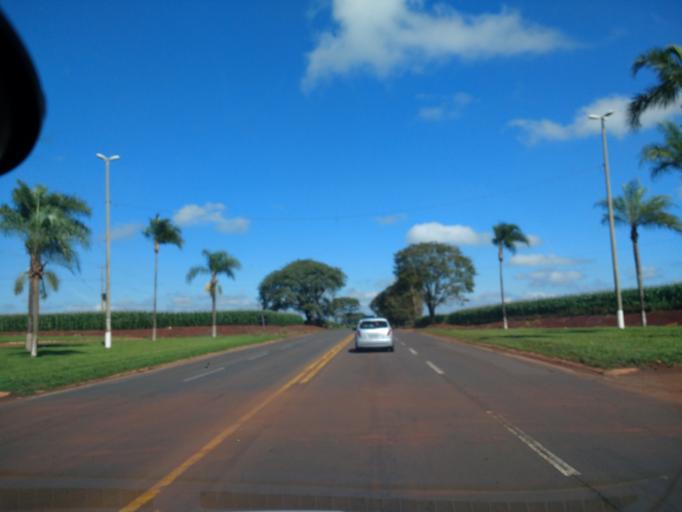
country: BR
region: Parana
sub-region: Cianorte
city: Cianorte
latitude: -23.6422
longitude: -52.4795
